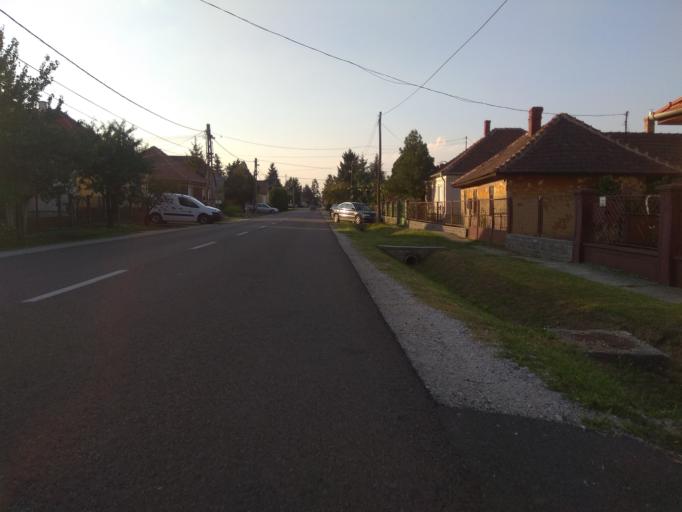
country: HU
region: Borsod-Abauj-Zemplen
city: Nyekladhaza
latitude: 47.9887
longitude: 20.8382
